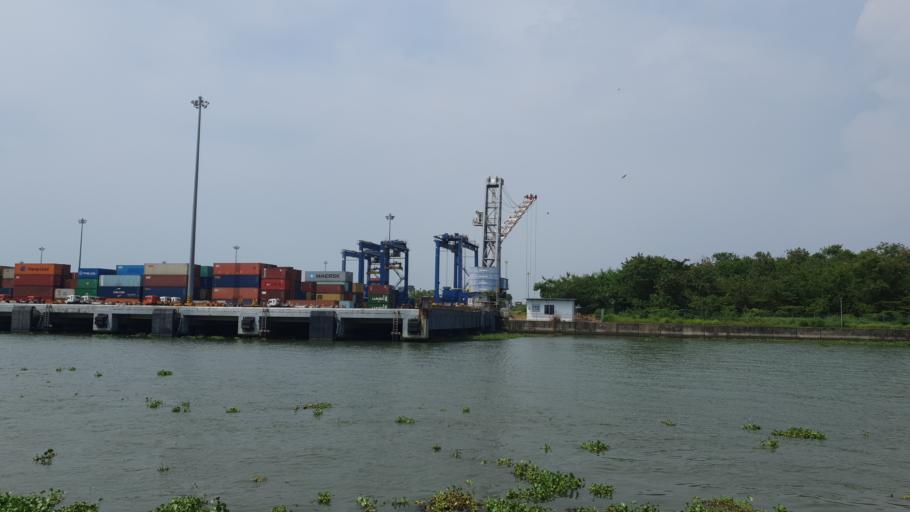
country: IN
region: Kerala
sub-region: Ernakulam
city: Cochin
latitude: 9.9783
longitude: 76.2551
